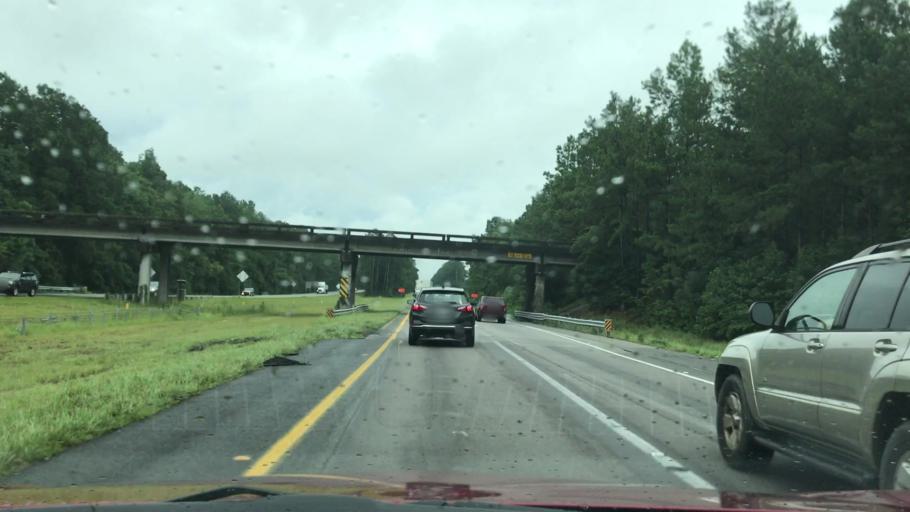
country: US
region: South Carolina
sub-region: Dorchester County
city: Ridgeville
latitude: 33.1123
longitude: -80.2624
